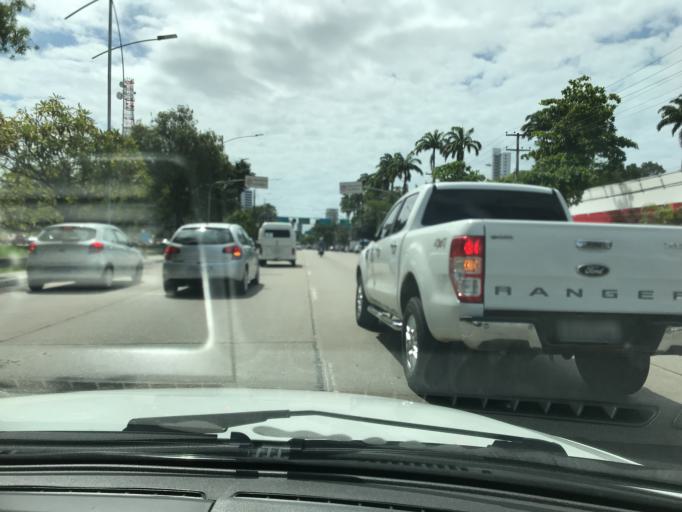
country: BR
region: Pernambuco
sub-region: Recife
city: Recife
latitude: -8.0544
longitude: -34.8971
